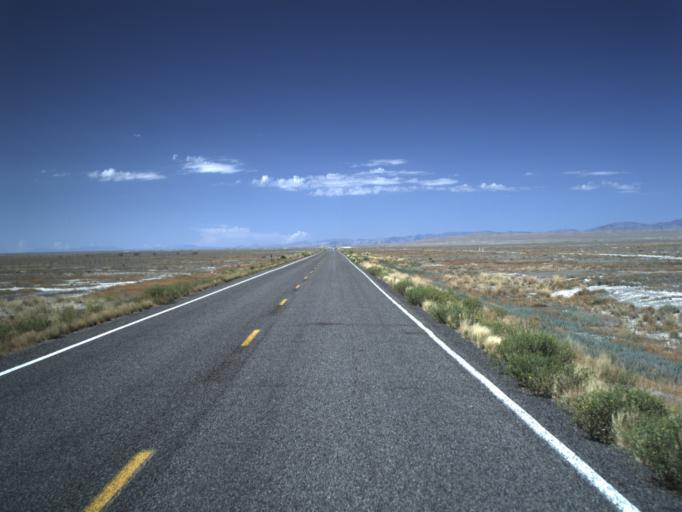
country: US
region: Utah
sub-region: Millard County
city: Delta
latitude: 39.2282
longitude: -112.9355
